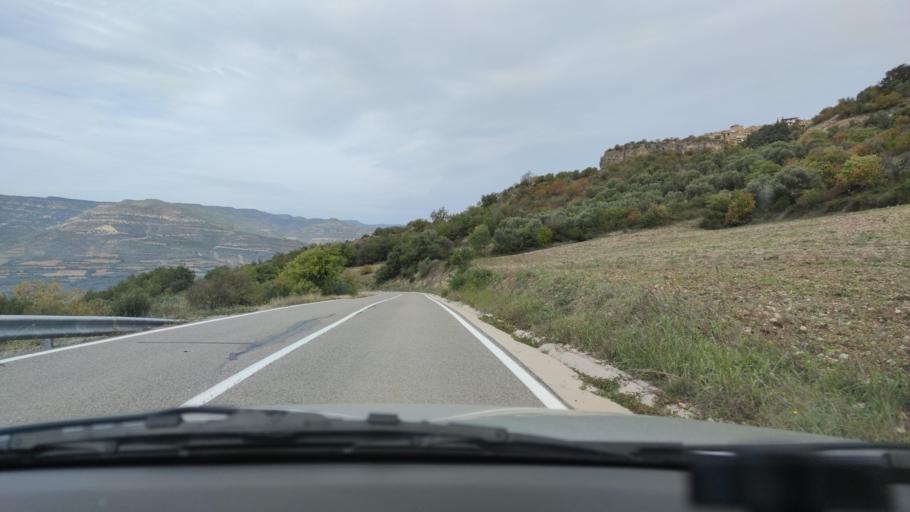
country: ES
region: Catalonia
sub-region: Provincia de Lleida
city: Llimiana
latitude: 42.0677
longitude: 0.9183
